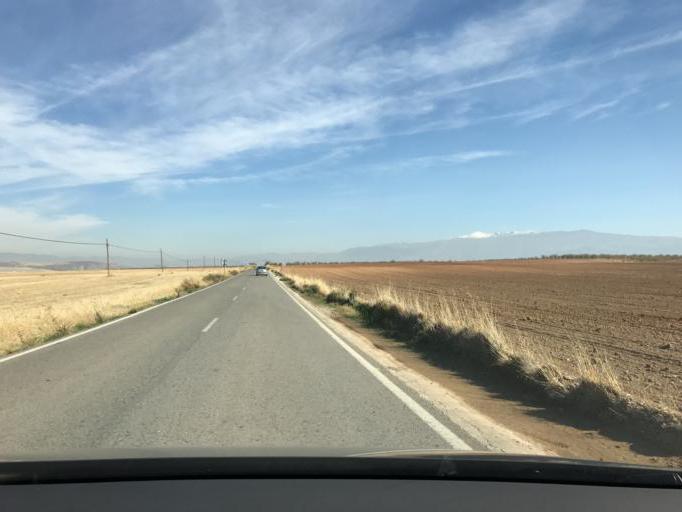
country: ES
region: Andalusia
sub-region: Provincia de Granada
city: Ventas de Huelma
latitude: 37.0768
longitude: -3.7905
